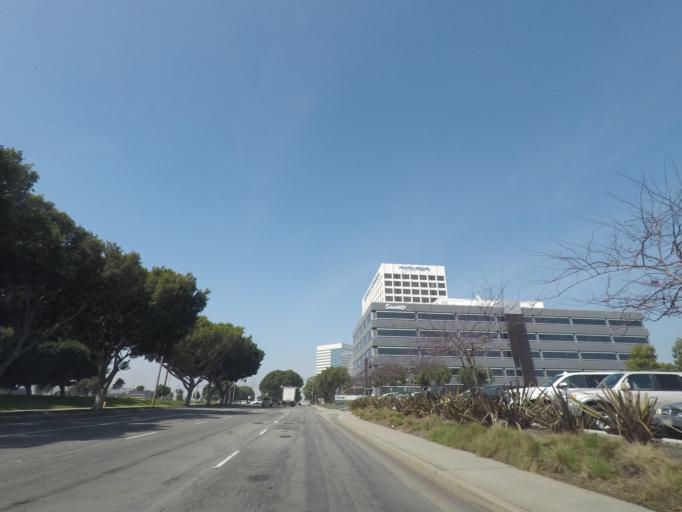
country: US
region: California
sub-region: Los Angeles County
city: Del Aire
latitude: 33.9165
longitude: -118.3894
